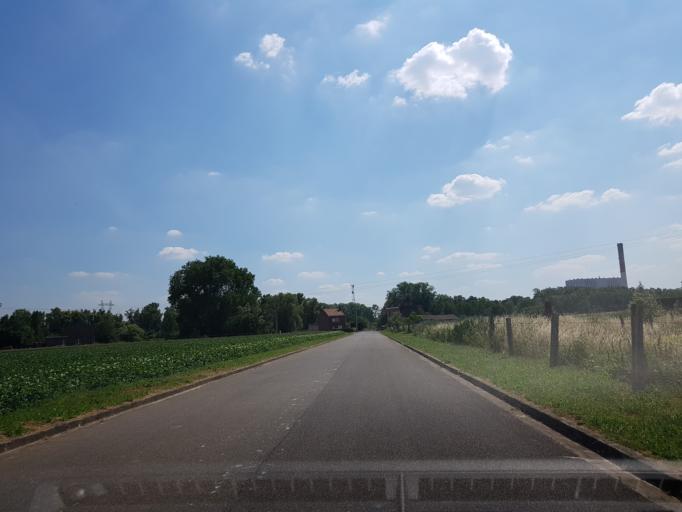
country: FR
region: Nord-Pas-de-Calais
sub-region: Departement du Nord
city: Roeulx
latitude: 50.3040
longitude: 3.3272
